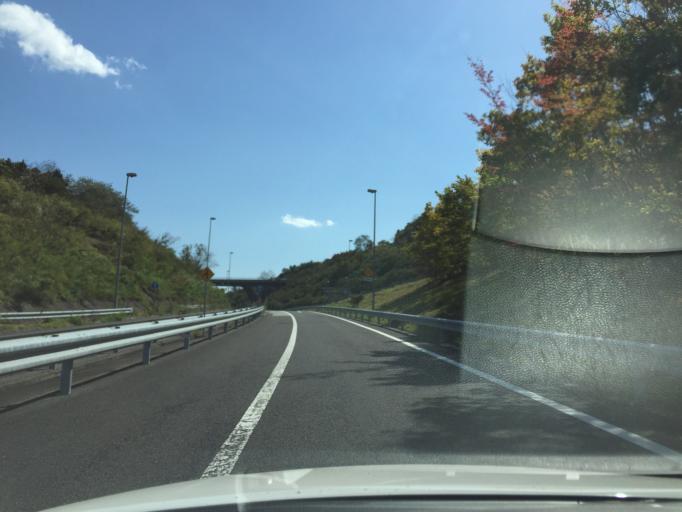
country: JP
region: Fukushima
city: Sukagawa
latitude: 37.1911
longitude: 140.2997
